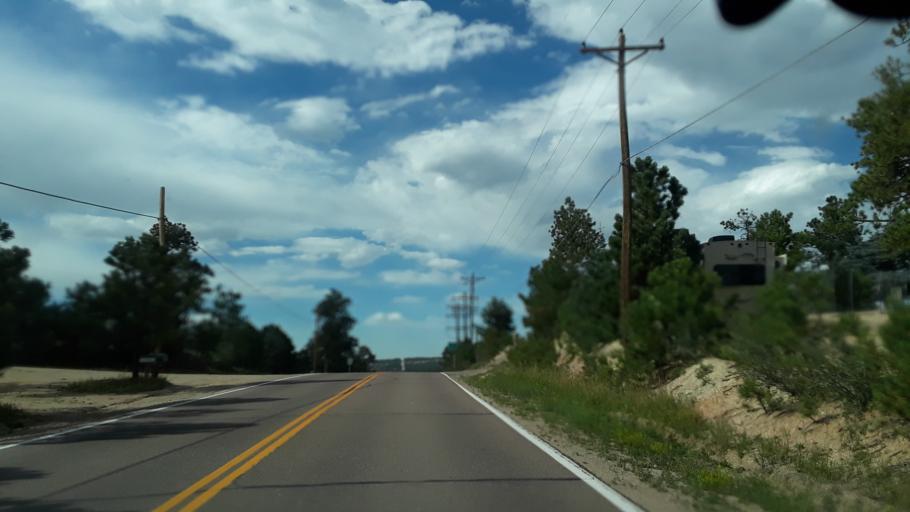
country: US
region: Colorado
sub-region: El Paso County
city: Black Forest
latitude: 38.9952
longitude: -104.7004
